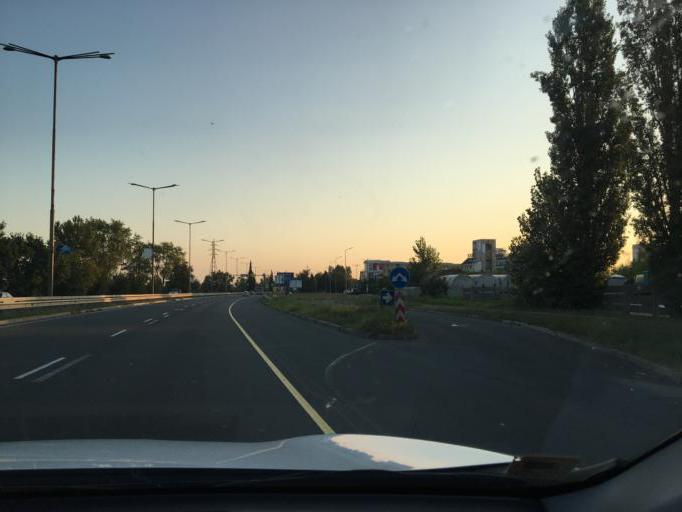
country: BG
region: Burgas
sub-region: Obshtina Burgas
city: Burgas
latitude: 42.4795
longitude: 27.4365
